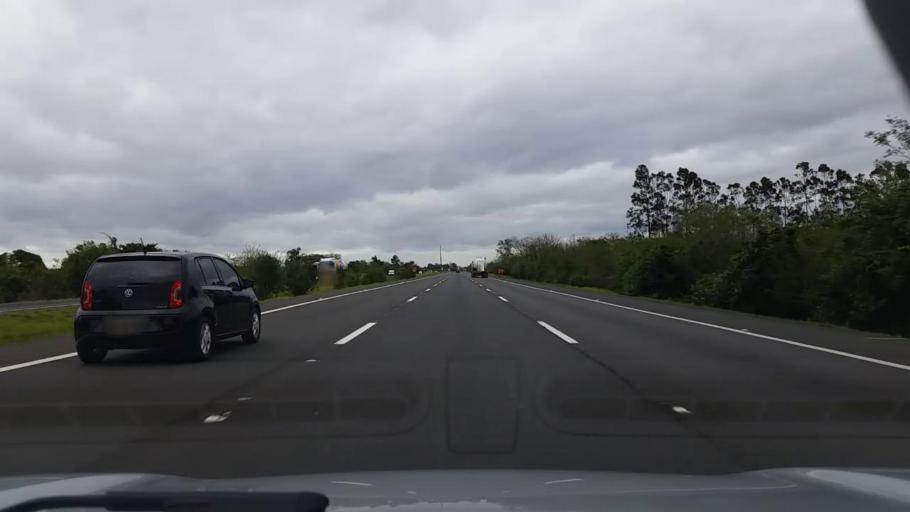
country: BR
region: Rio Grande do Sul
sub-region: Rolante
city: Rolante
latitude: -29.8837
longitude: -50.5568
